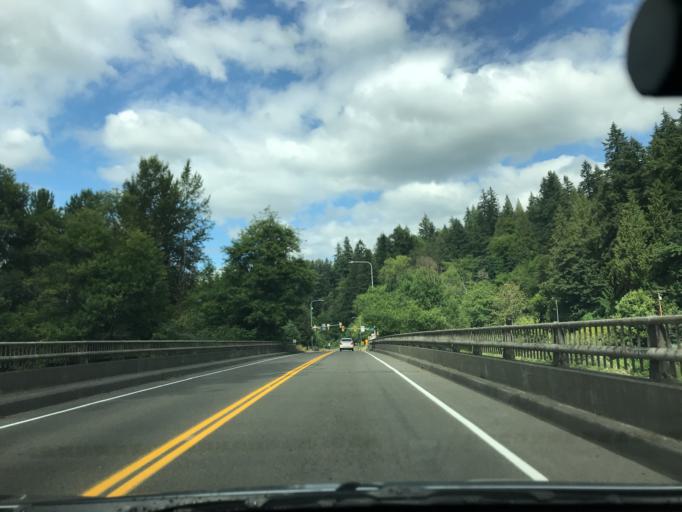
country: US
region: Washington
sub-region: King County
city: Lea Hill
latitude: 47.3015
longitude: -122.1759
